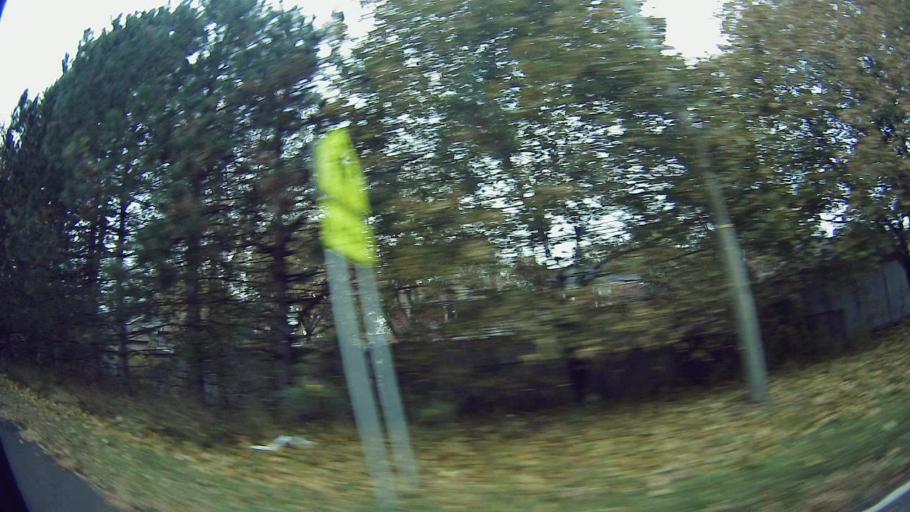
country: US
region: Michigan
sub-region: Wayne County
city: Dearborn Heights
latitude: 42.3209
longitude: -83.2726
